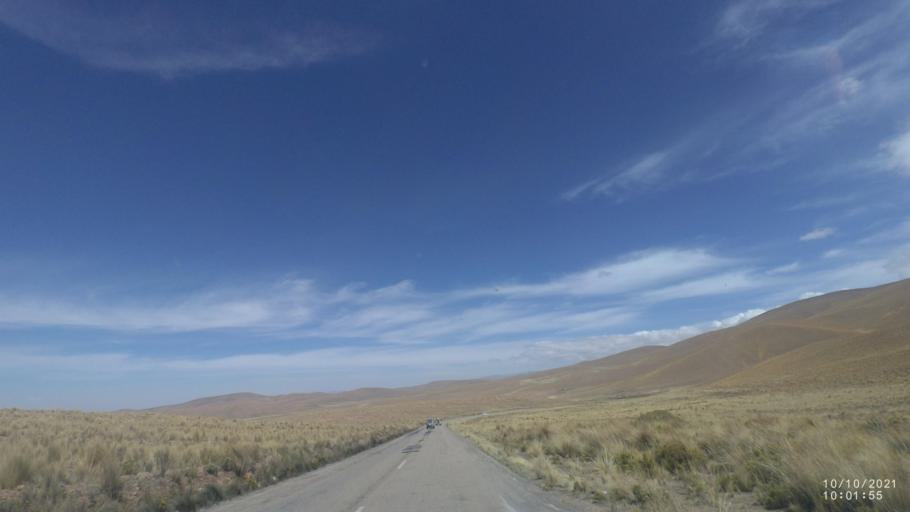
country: BO
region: La Paz
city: Eucaliptus
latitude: -17.3642
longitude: -67.4274
